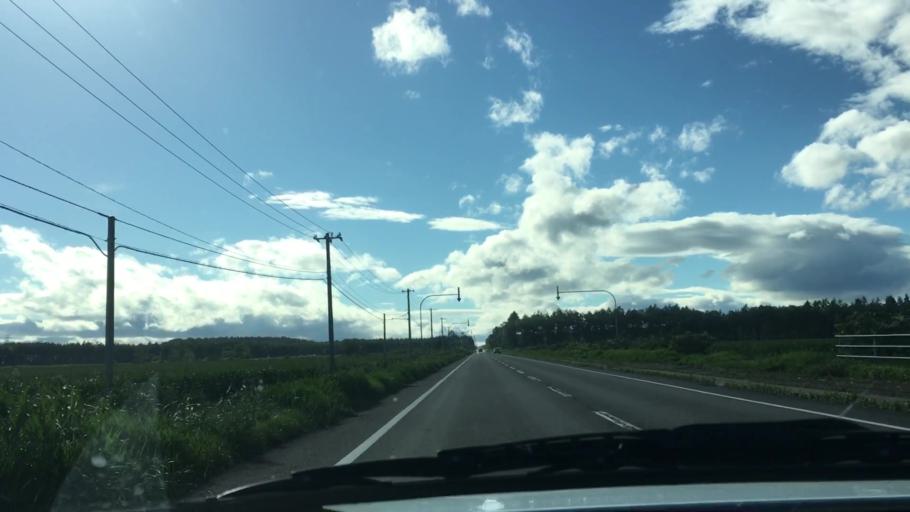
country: JP
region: Hokkaido
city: Otofuke
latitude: 43.1606
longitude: 143.1628
